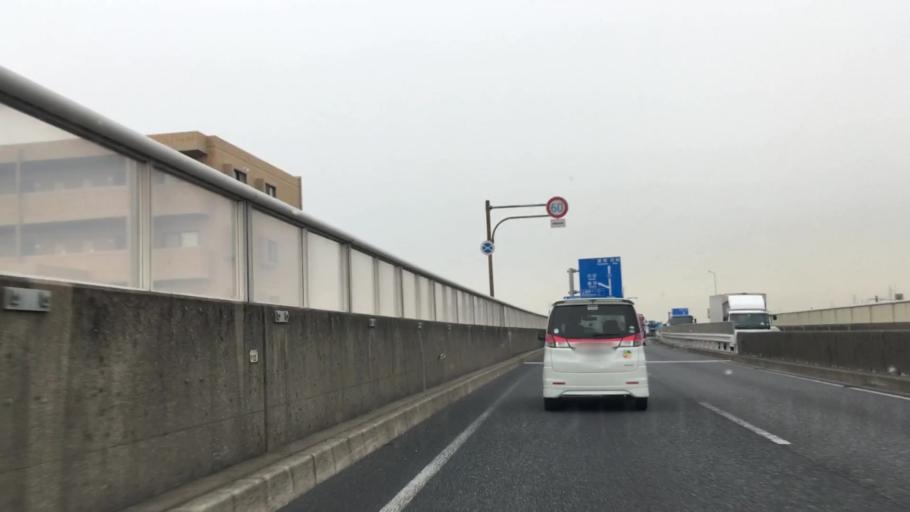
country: JP
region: Aichi
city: Chiryu
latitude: 35.0116
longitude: 137.0242
